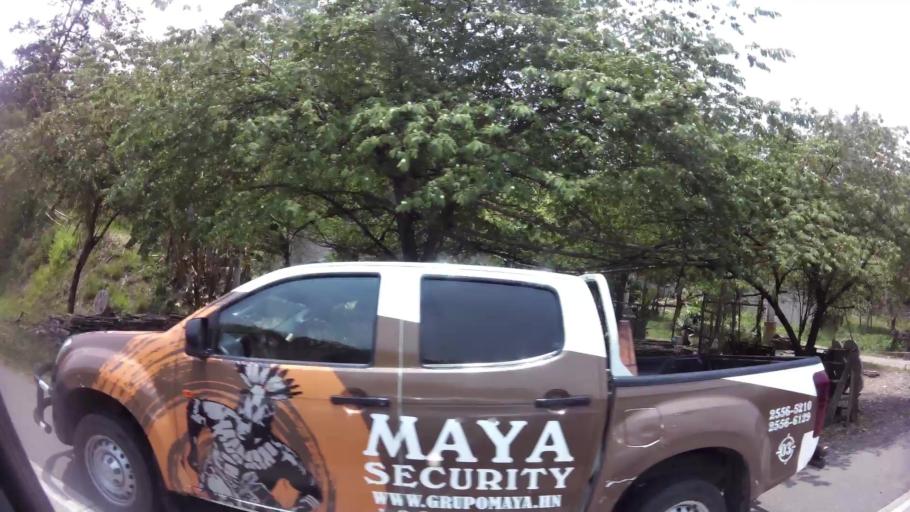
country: HN
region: Comayagua
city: Taulabe
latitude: 14.6833
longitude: -87.9542
